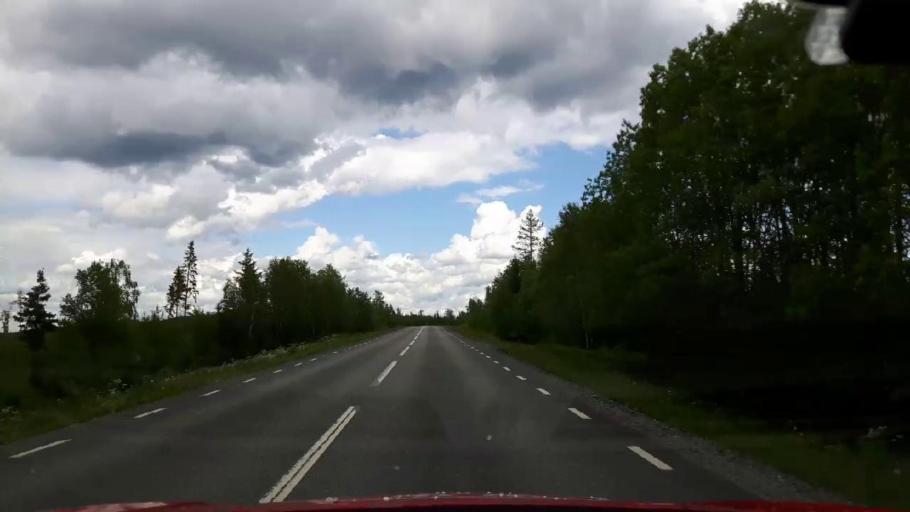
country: SE
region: Jaemtland
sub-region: Krokoms Kommun
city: Krokom
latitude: 63.7831
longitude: 14.3525
